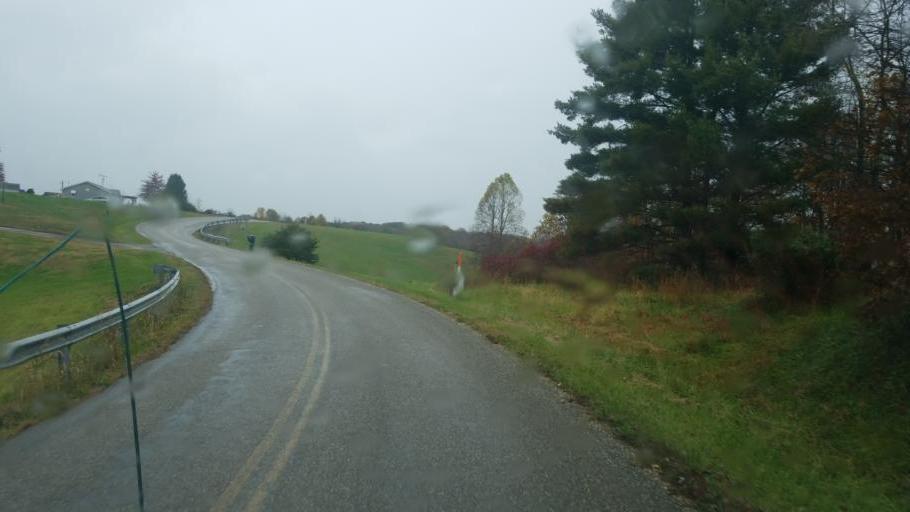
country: US
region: West Virginia
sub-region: Wood County
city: Vienna
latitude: 39.3455
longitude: -81.6265
